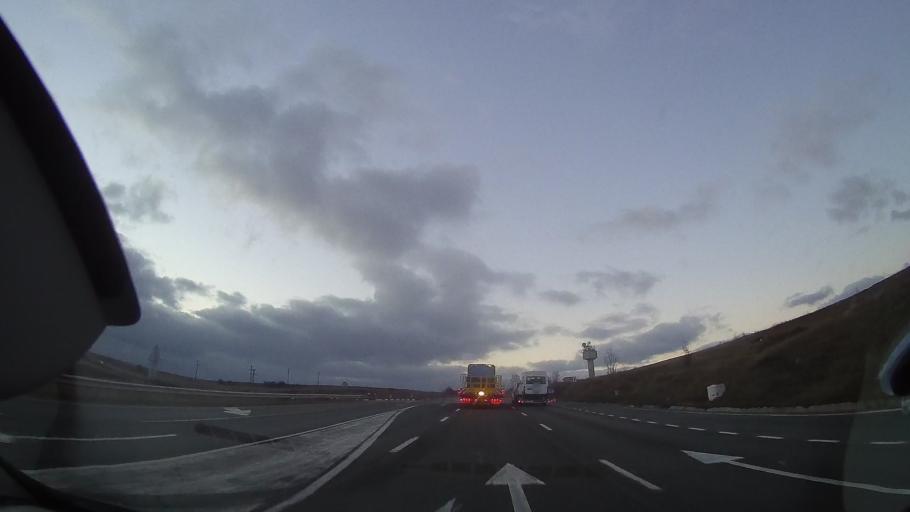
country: RO
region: Cluj
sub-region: Comuna Izvoru Crisului
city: Izvoru Crisului
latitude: 46.8243
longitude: 23.1575
